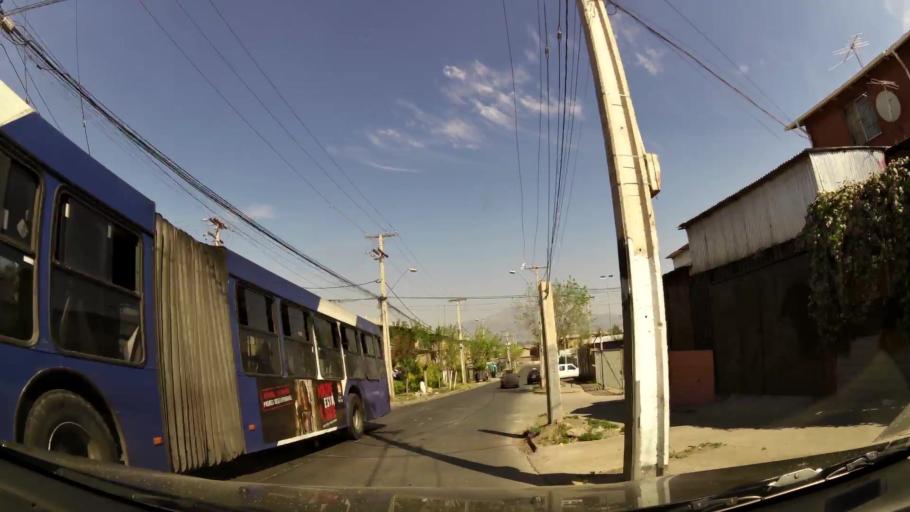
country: CL
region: Santiago Metropolitan
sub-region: Provincia de Cordillera
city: Puente Alto
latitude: -33.6276
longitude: -70.6073
